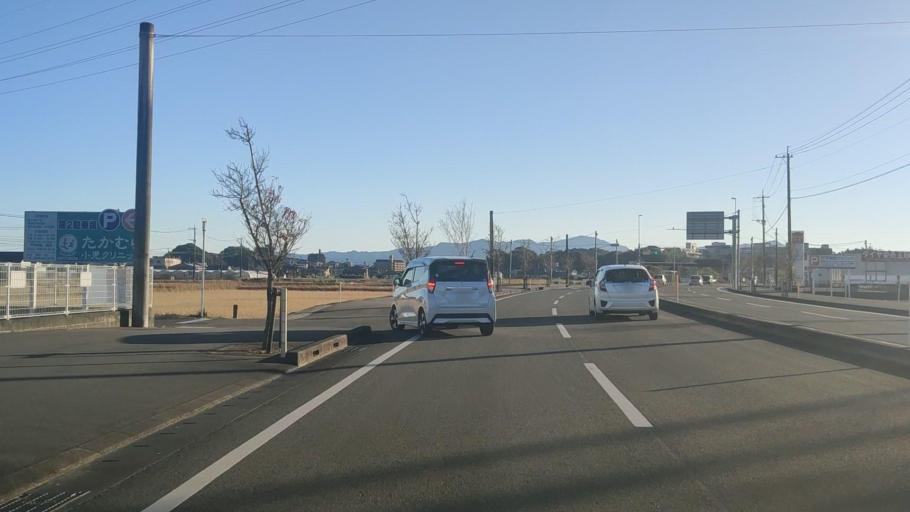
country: JP
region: Miyazaki
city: Miyazaki-shi
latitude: 31.8947
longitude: 131.4070
